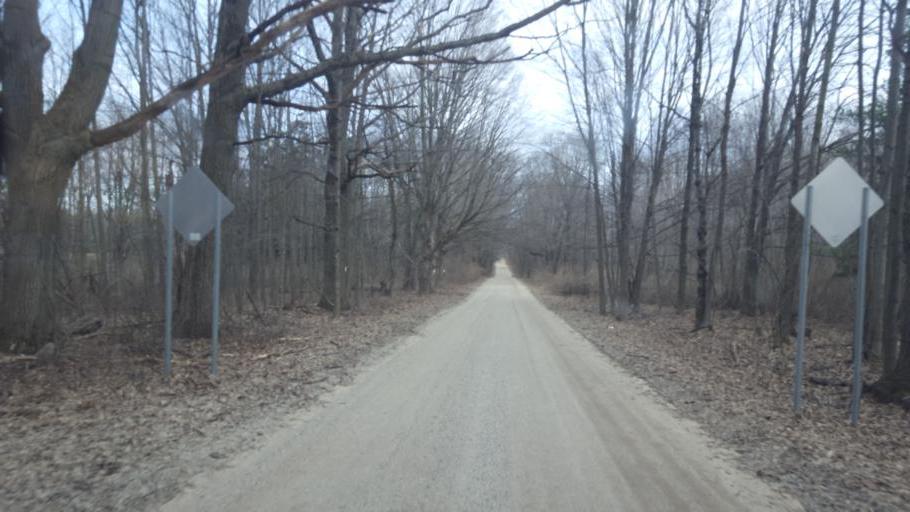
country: US
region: Michigan
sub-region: Isabella County
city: Lake Isabella
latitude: 43.6828
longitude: -85.1439
